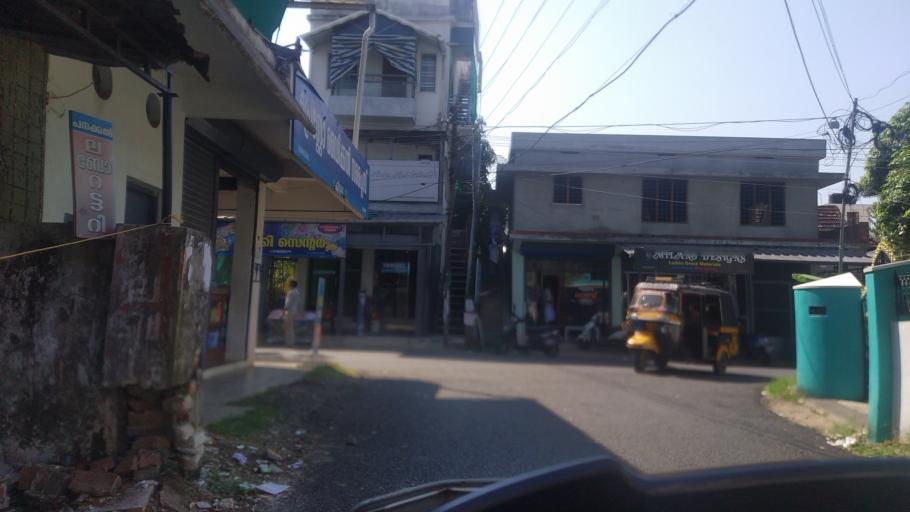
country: IN
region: Kerala
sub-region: Ernakulam
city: Elur
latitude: 10.0426
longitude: 76.2218
